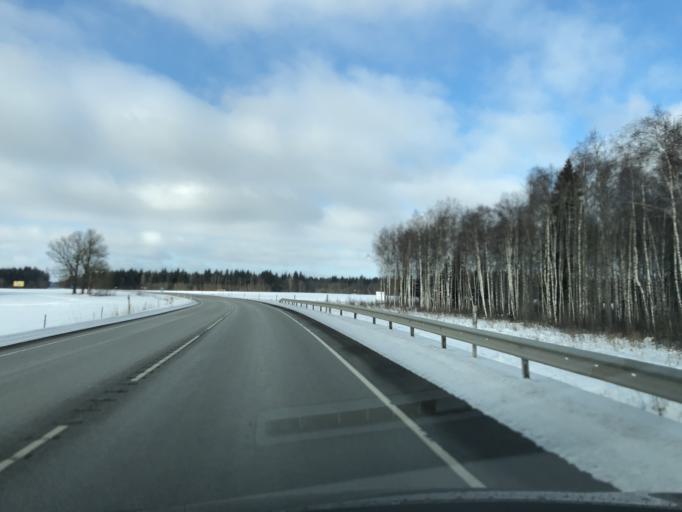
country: EE
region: Jaervamaa
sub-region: Paide linn
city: Paide
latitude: 58.8923
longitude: 25.6697
